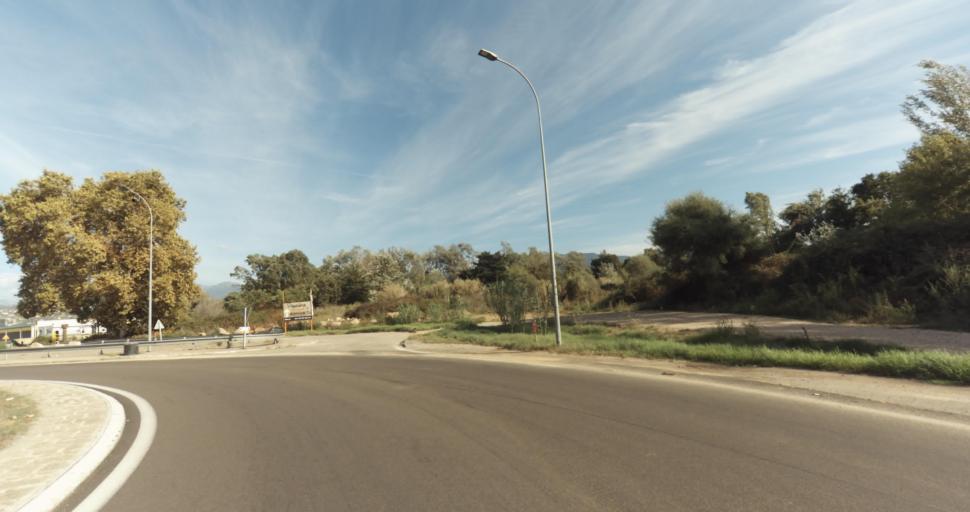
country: FR
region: Corsica
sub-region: Departement de la Corse-du-Sud
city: Afa
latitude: 41.9273
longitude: 8.7966
